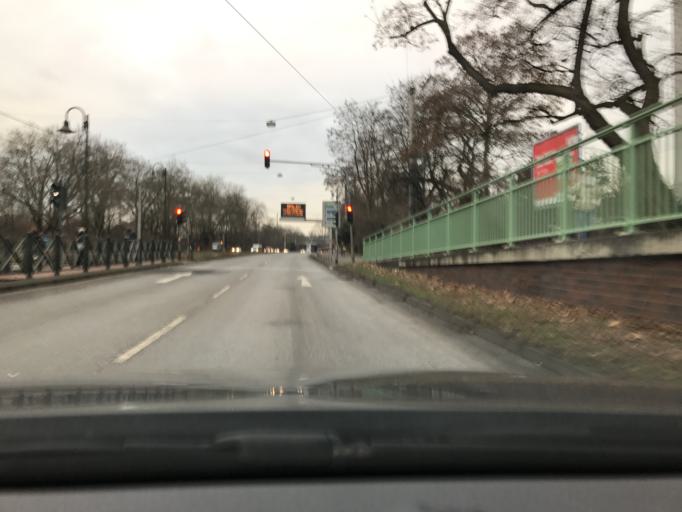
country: DE
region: North Rhine-Westphalia
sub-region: Regierungsbezirk Koln
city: Buchforst
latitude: 50.9483
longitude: 6.9928
